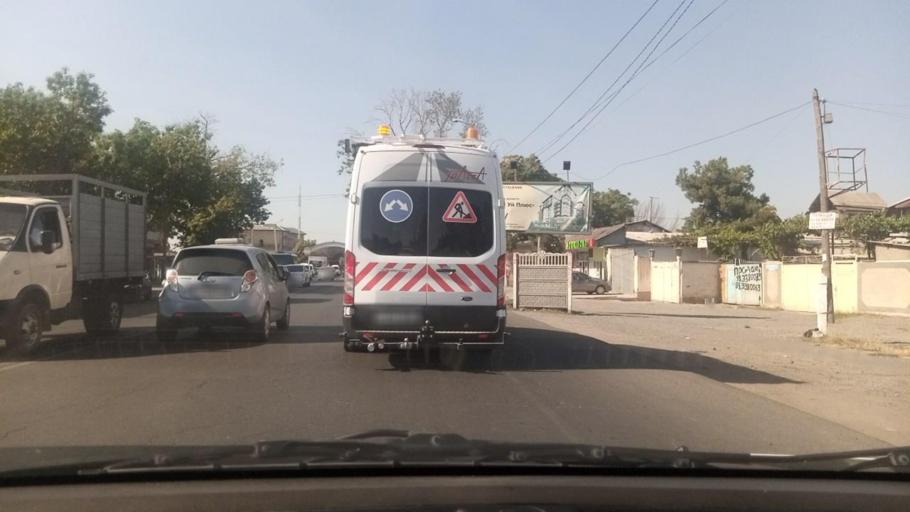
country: UZ
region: Toshkent Shahri
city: Bektemir
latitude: 41.2276
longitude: 69.3357
